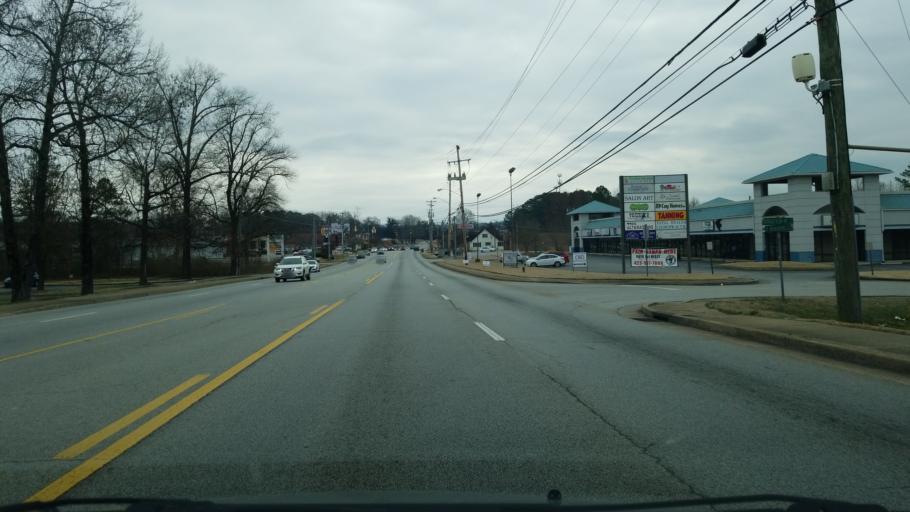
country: US
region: Tennessee
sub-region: Hamilton County
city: East Brainerd
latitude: 35.0132
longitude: -85.1601
